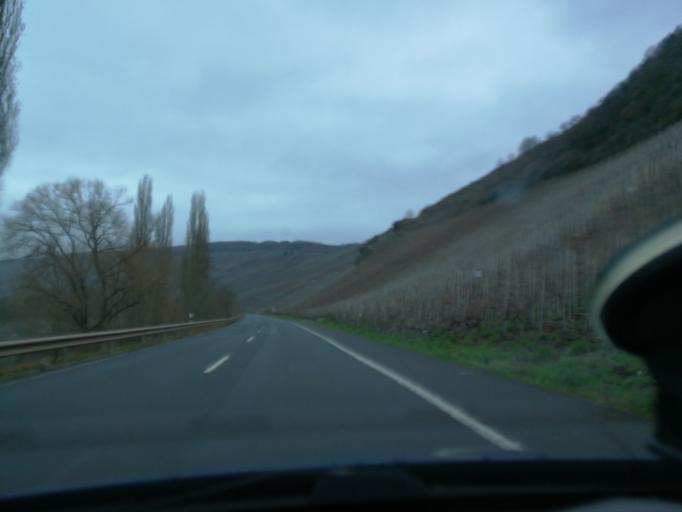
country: DE
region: Rheinland-Pfalz
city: Kowerich
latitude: 49.8360
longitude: 6.8818
